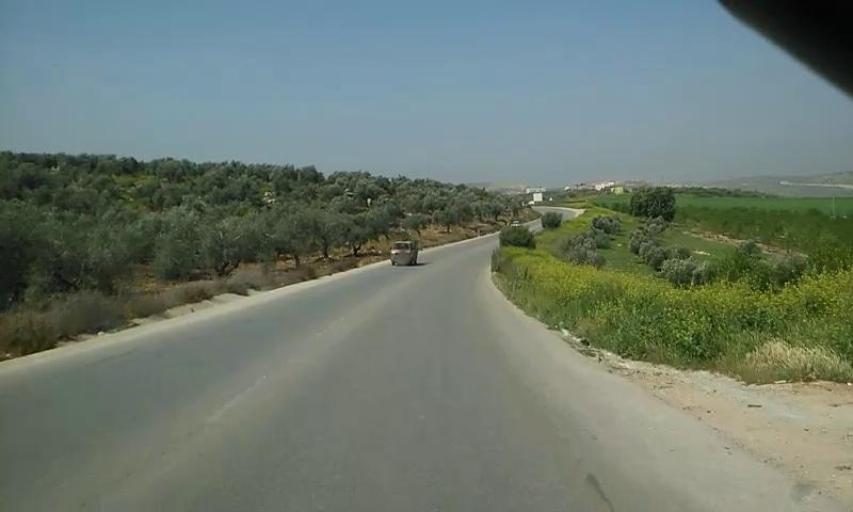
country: PS
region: West Bank
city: Az Zababidah
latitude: 32.3763
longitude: 35.3342
